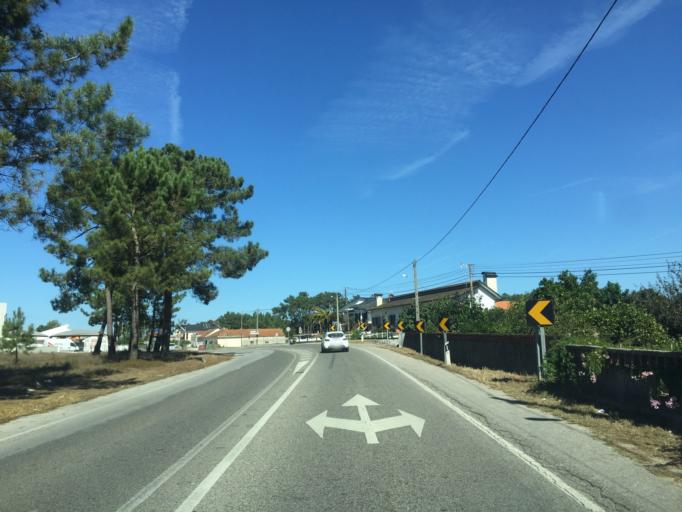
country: PT
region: Coimbra
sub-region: Figueira da Foz
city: Alhadas
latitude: 40.2566
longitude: -8.7802
